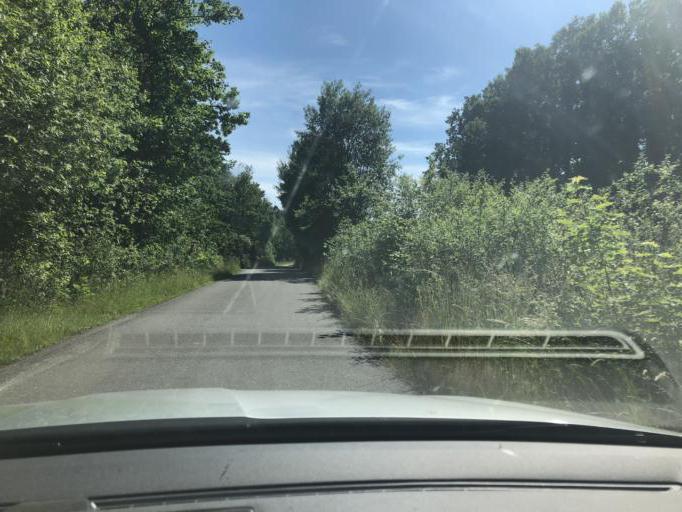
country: SE
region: Blekinge
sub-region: Karlshamns Kommun
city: Karlshamn
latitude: 56.1657
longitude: 14.8053
